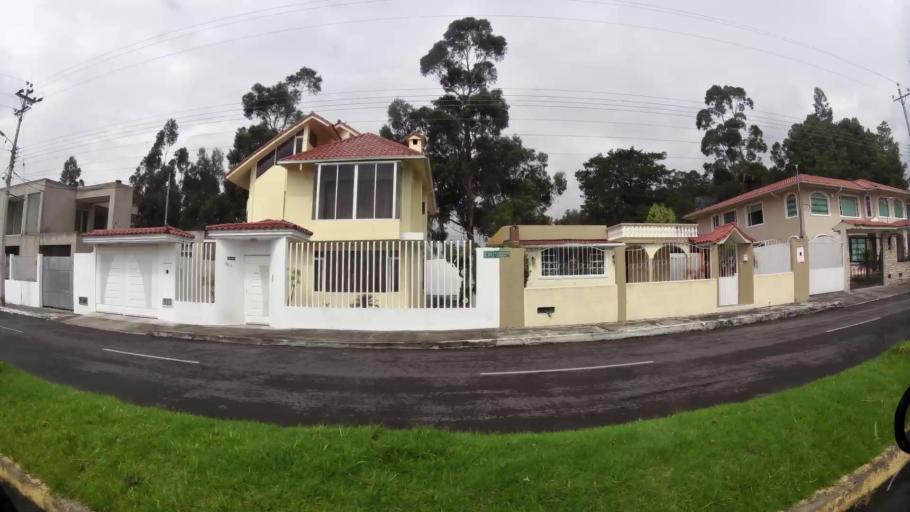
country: EC
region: Pichincha
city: Sangolqui
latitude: -0.3093
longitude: -78.4740
